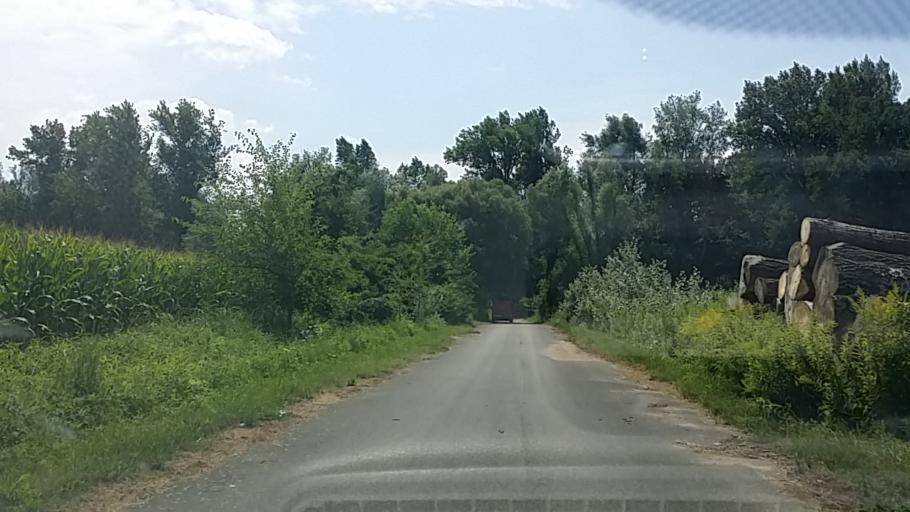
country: HR
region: Medimurska
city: Kotoriba
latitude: 46.3775
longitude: 16.8341
